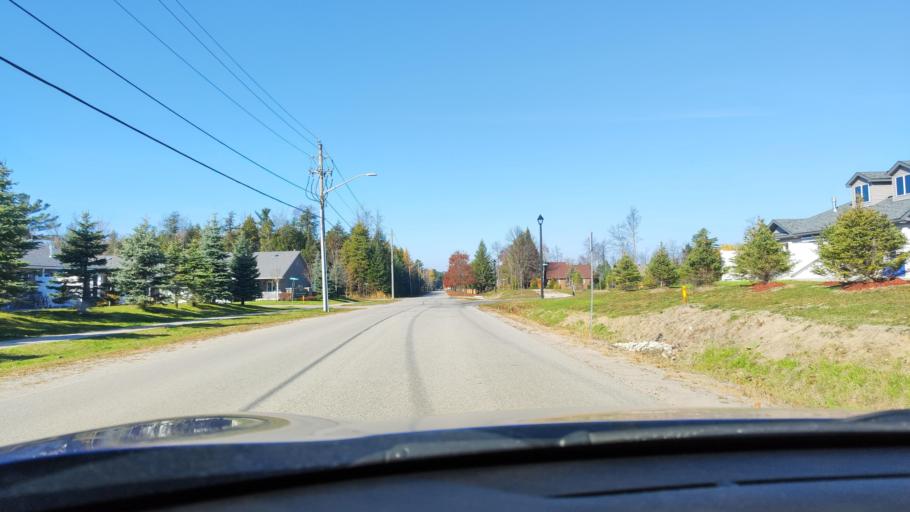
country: CA
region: Ontario
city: Wasaga Beach
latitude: 44.5295
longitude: -79.9978
